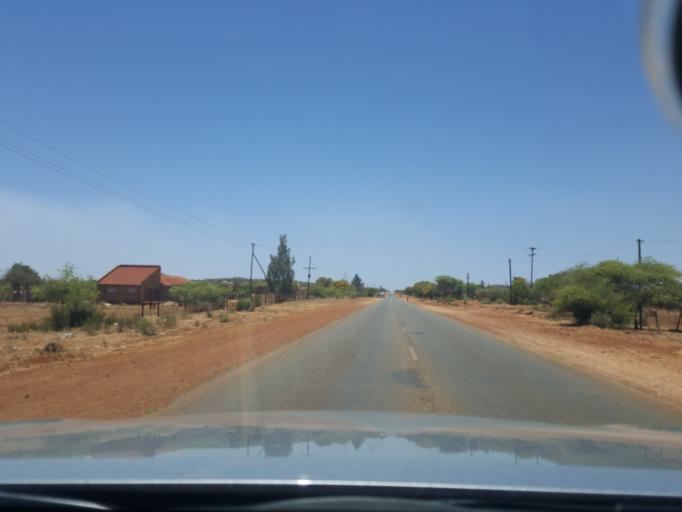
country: ZA
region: North-West
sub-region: Ngaka Modiri Molema District Municipality
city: Zeerust
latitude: -25.4457
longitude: 25.9655
